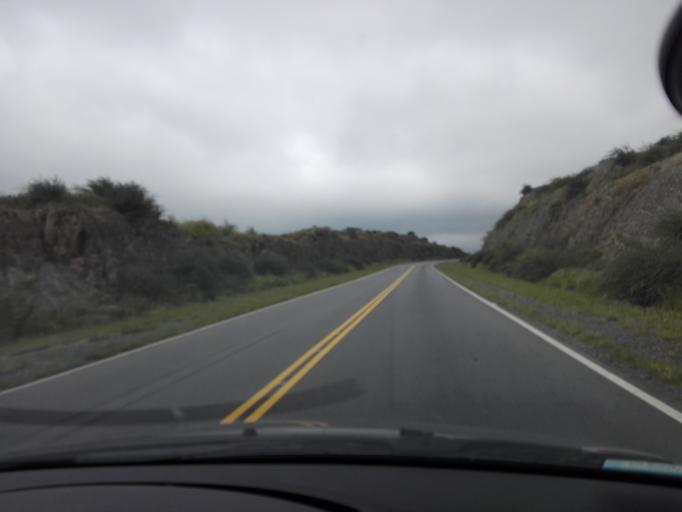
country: AR
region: Cordoba
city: Cuesta Blanca
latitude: -31.6253
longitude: -64.6726
